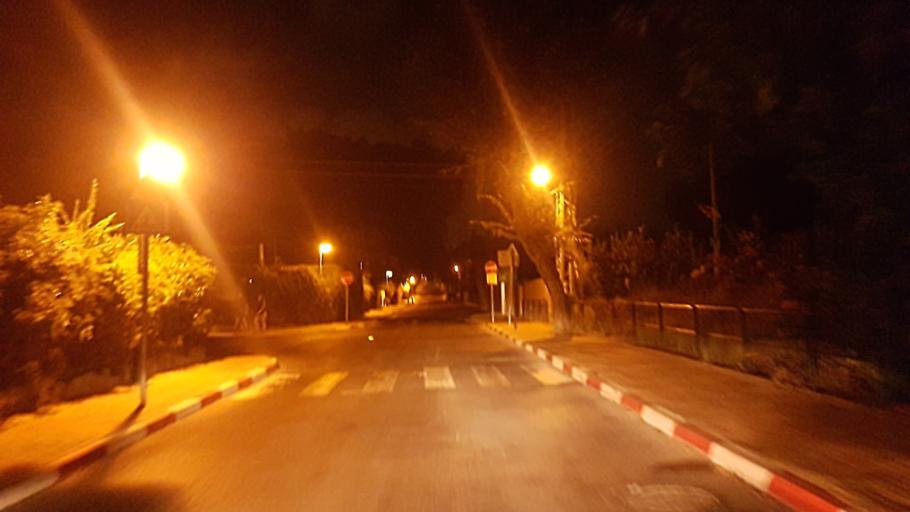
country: IL
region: Central District
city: Hod HaSharon
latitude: 32.1644
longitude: 34.8867
